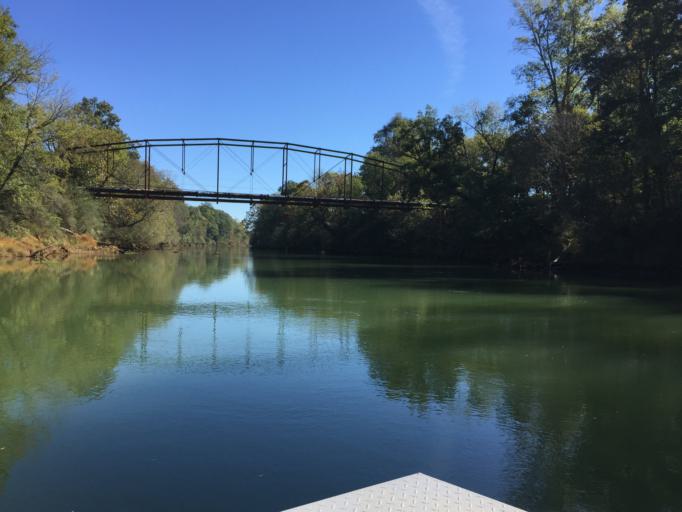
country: US
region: Georgia
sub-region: Gwinnett County
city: Duluth
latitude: 34.0298
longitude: -84.1423
